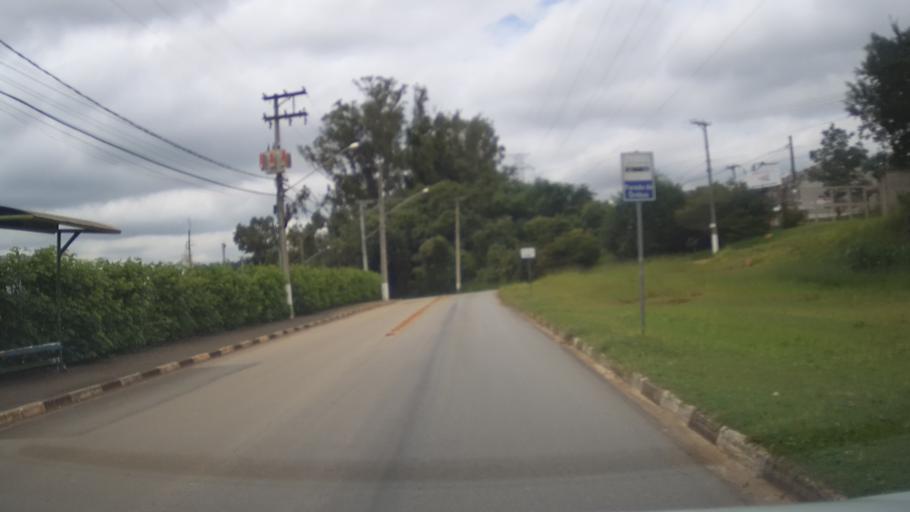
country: BR
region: Sao Paulo
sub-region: Louveira
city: Louveira
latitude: -23.0740
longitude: -46.9898
